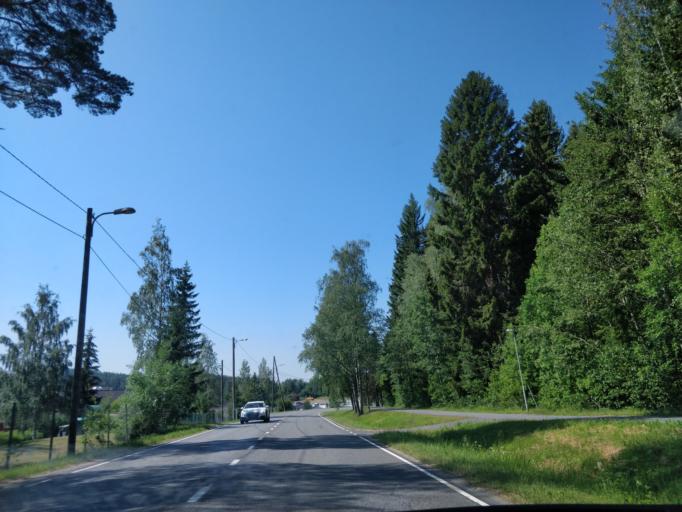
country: FI
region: Haeme
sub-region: Haemeenlinna
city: Tervakoski
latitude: 60.8084
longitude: 24.6110
